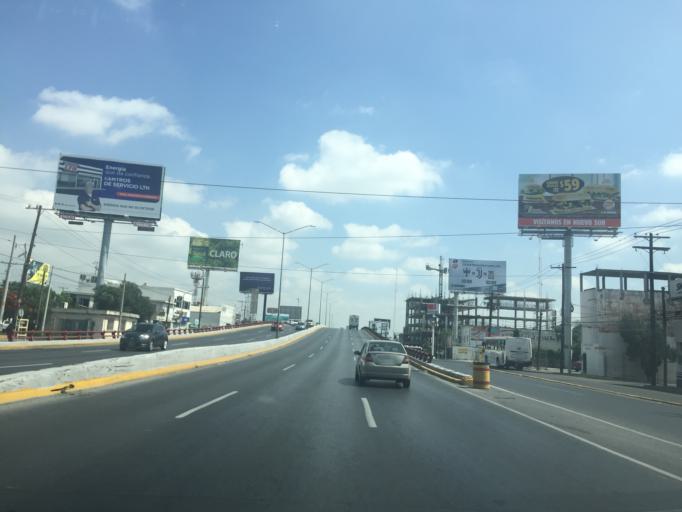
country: MX
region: Nuevo Leon
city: Guadalupe
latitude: 25.6647
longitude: -100.2840
